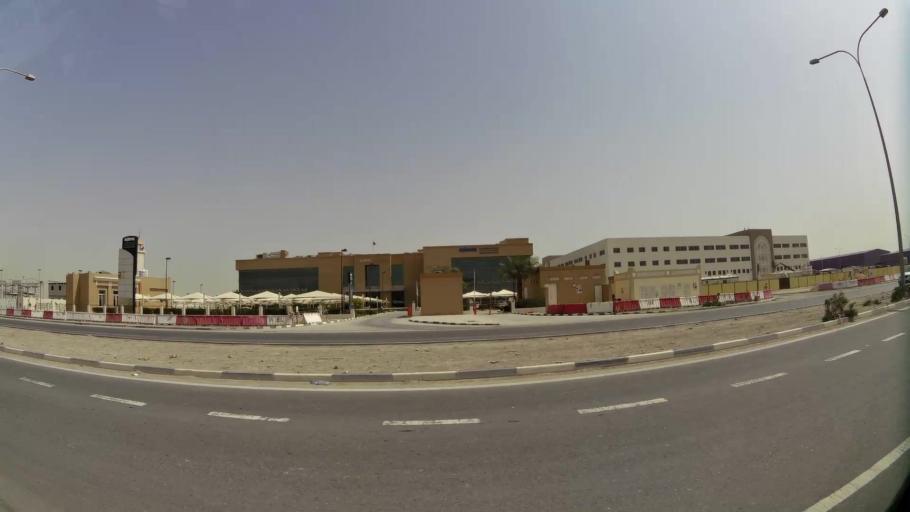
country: QA
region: Baladiyat ar Rayyan
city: Ar Rayyan
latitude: 25.1662
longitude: 51.4033
